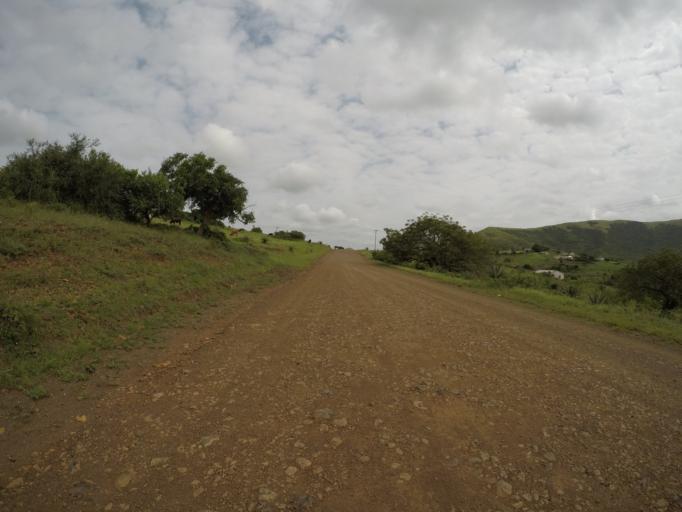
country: ZA
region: KwaZulu-Natal
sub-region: uThungulu District Municipality
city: Empangeni
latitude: -28.6155
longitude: 31.9004
